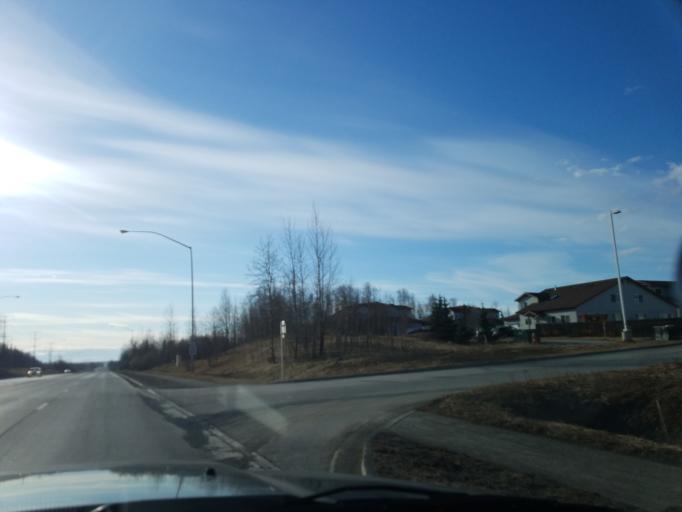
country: US
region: Alaska
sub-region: Anchorage Municipality
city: Elmendorf Air Force Base
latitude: 61.1808
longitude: -149.7511
